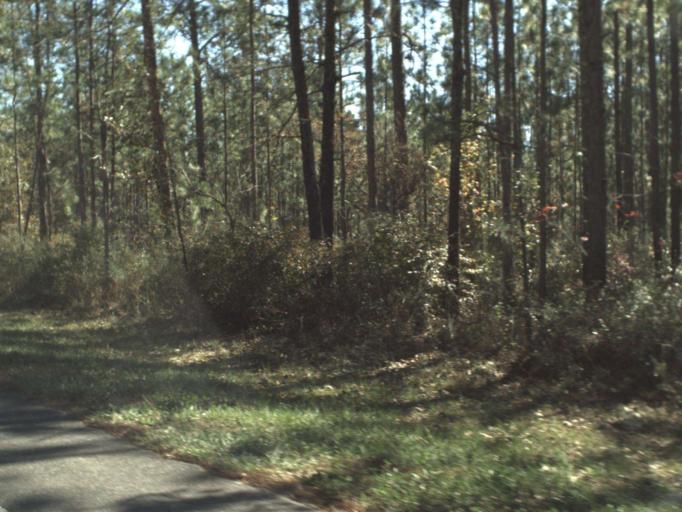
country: US
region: Florida
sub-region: Okaloosa County
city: Crestview
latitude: 30.8501
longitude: -86.7674
